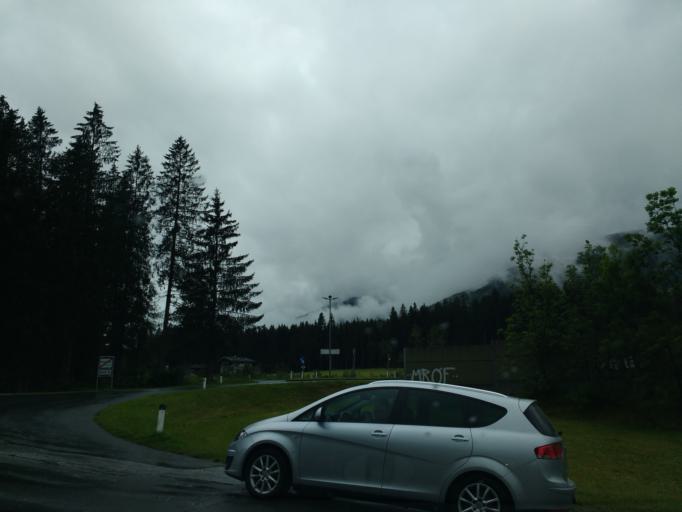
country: AT
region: Salzburg
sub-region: Politischer Bezirk Zell am See
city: Neukirchen am Grossvenediger
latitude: 47.2482
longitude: 12.2725
